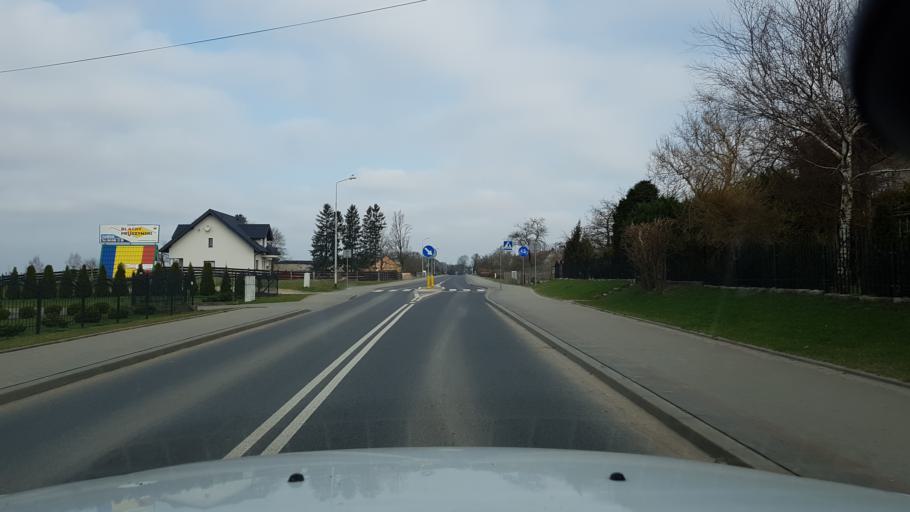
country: PL
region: West Pomeranian Voivodeship
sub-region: Powiat koszalinski
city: Sianow
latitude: 54.2536
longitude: 16.2766
